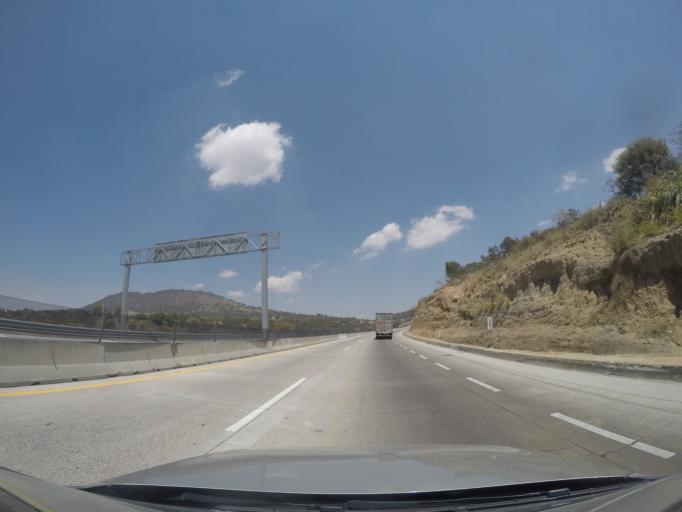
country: MX
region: Tlaxcala
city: Espanita
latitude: 19.4610
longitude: -98.4514
